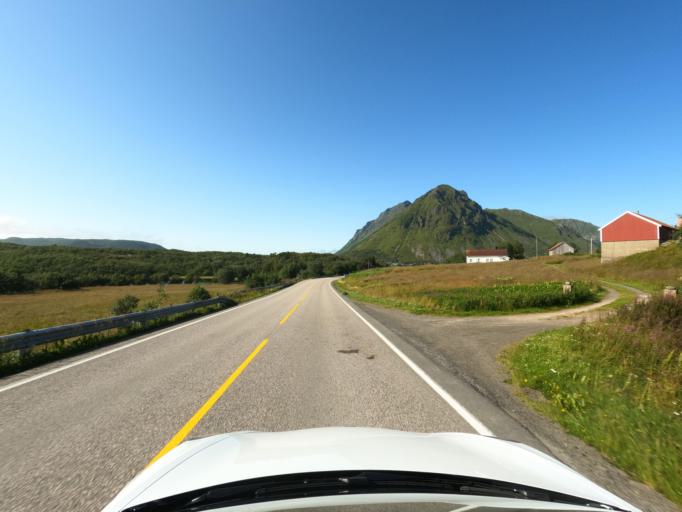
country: NO
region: Nordland
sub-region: Vestvagoy
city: Evjen
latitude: 68.2632
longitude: 13.9816
